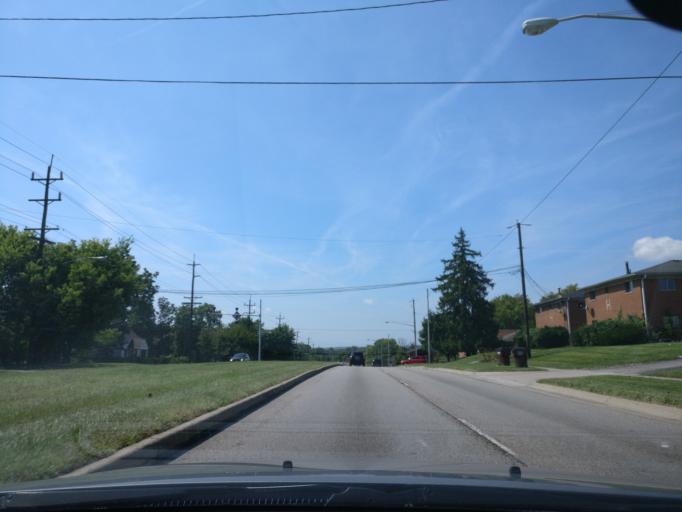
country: US
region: Ohio
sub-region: Butler County
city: Mayfield
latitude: 39.4997
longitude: -84.3581
